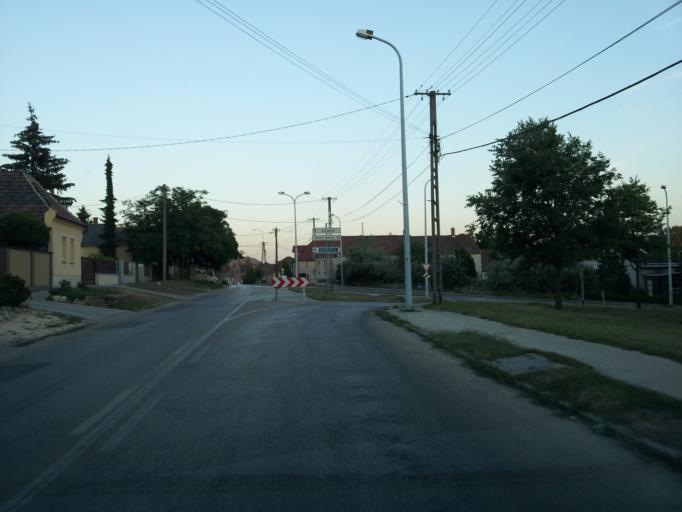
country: HU
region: Komarom-Esztergom
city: Tatabanya
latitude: 47.5751
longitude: 18.4110
